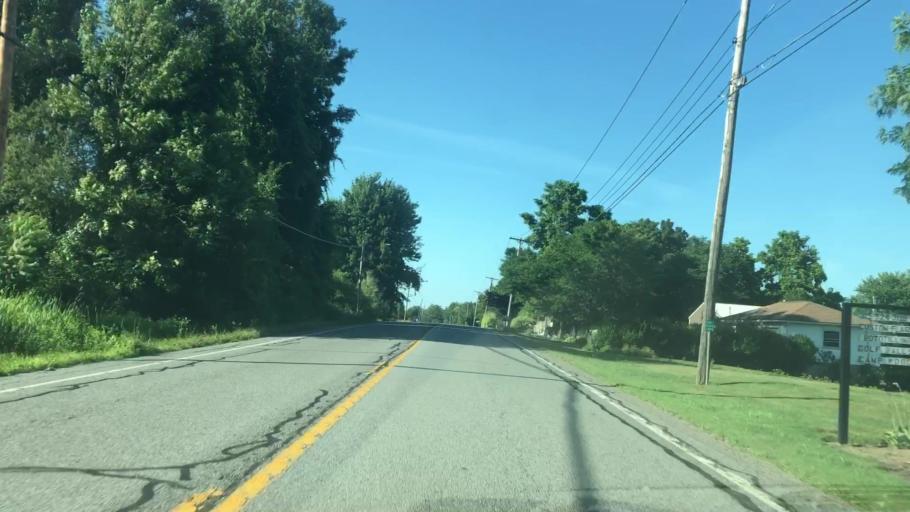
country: US
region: New York
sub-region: Wayne County
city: Ontario
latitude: 43.1743
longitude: -77.2870
